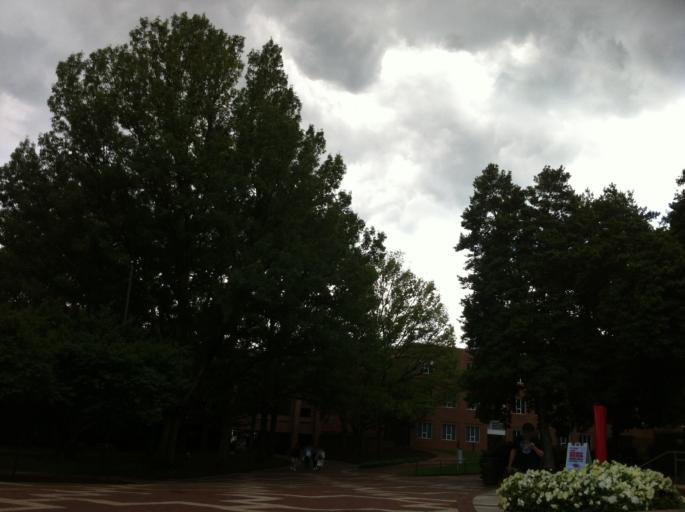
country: US
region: North Carolina
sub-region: Wake County
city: West Raleigh
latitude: 35.7873
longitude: -78.6707
